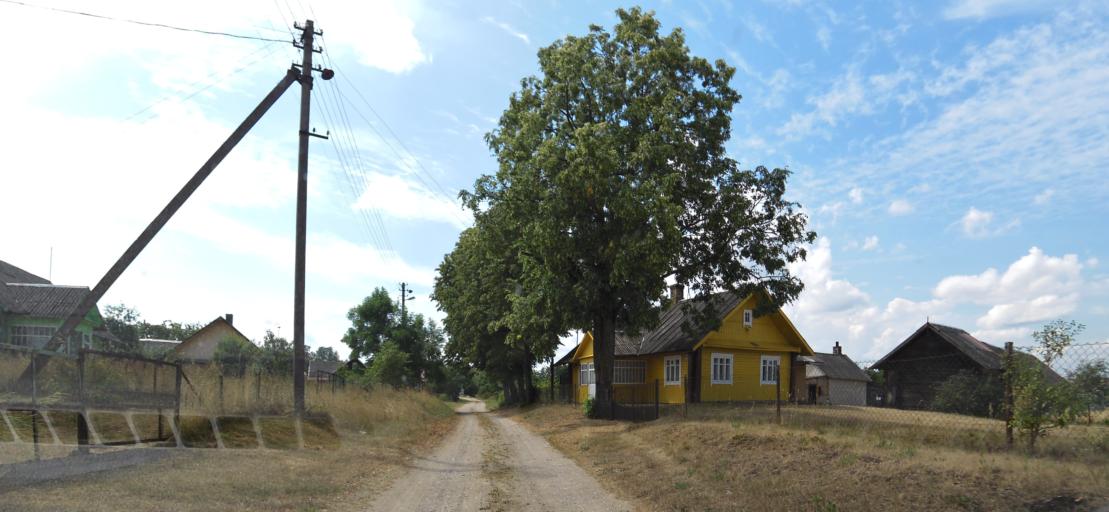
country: LT
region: Vilnius County
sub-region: Trakai
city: Rudiskes
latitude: 54.2951
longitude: 24.7834
